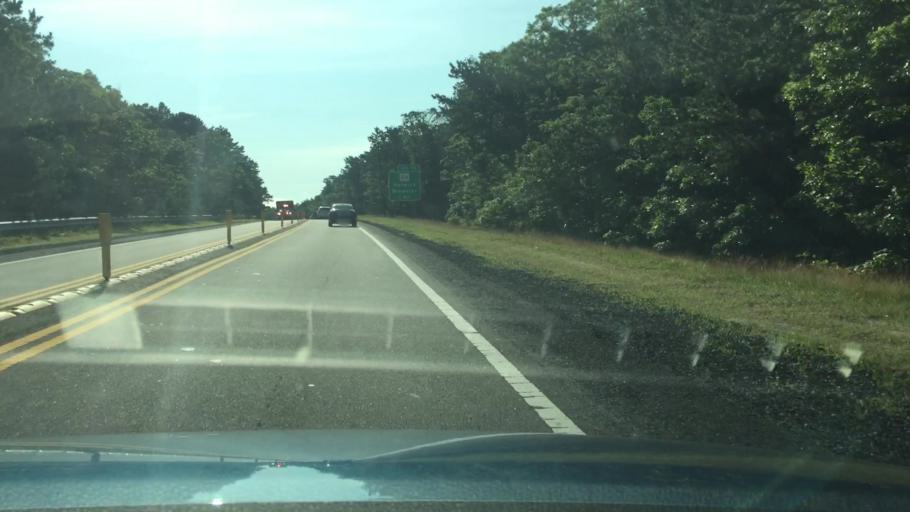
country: US
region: Massachusetts
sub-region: Barnstable County
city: Northwest Harwich
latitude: 41.6995
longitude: -70.1034
